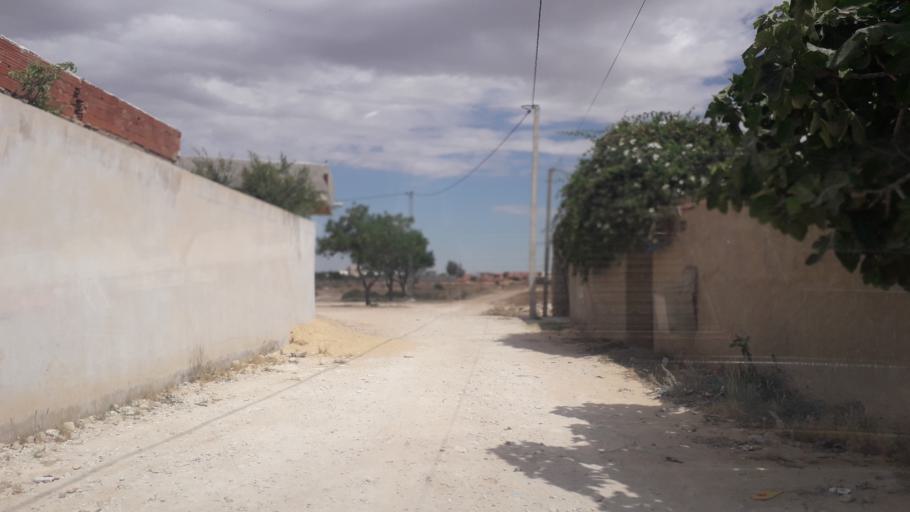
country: TN
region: Safaqis
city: Al Qarmadah
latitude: 34.8425
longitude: 10.7737
